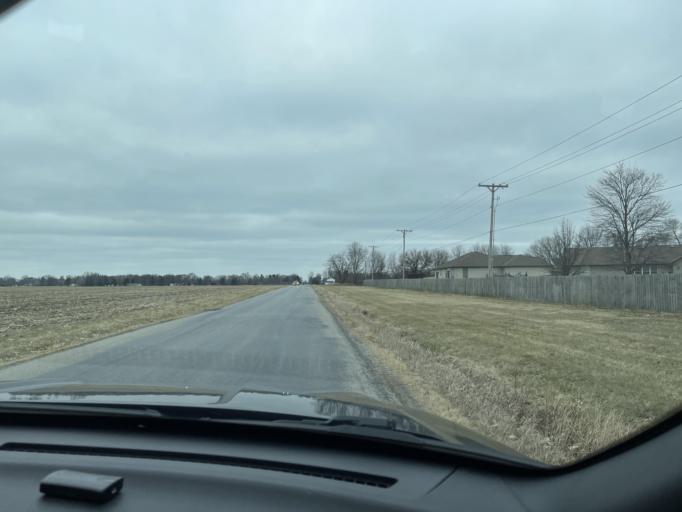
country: US
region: Illinois
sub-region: Sangamon County
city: Jerome
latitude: 39.7766
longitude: -89.7534
